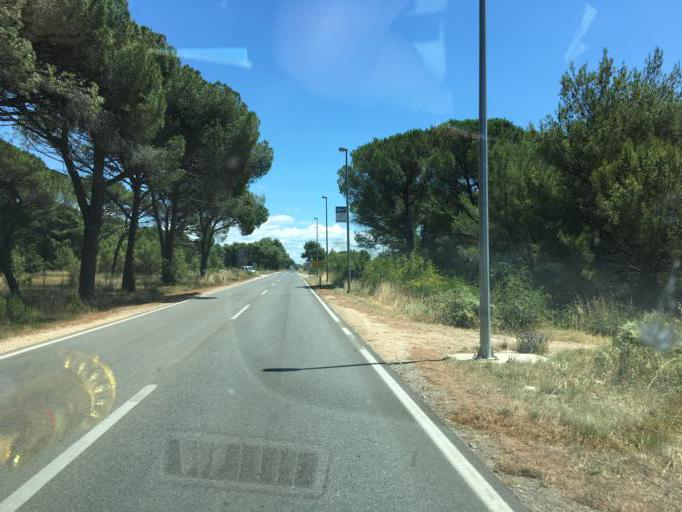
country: HR
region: Zadarska
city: Biograd na Moru
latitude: 43.9414
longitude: 15.4608
